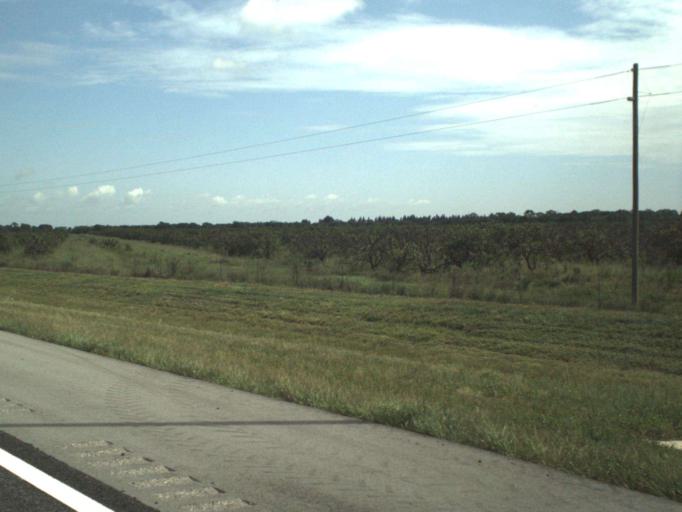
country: US
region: Florida
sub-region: Saint Lucie County
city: Lakewood Park
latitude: 27.5068
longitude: -80.4440
